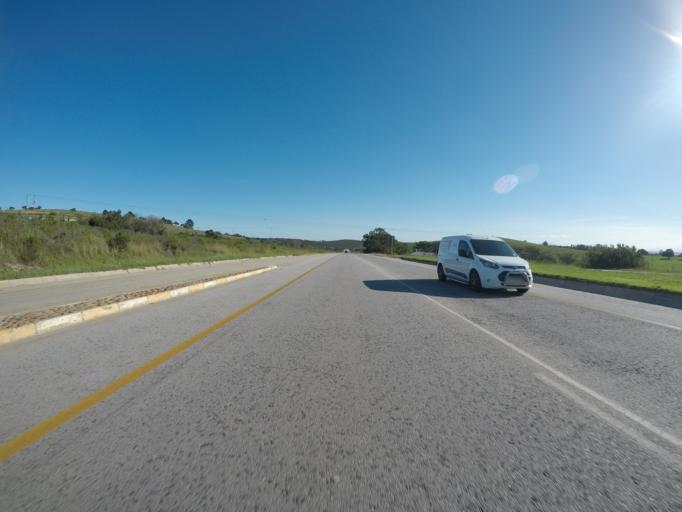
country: ZA
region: Eastern Cape
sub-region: Cacadu District Municipality
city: Jeffrey's Bay
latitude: -33.8984
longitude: 25.1189
